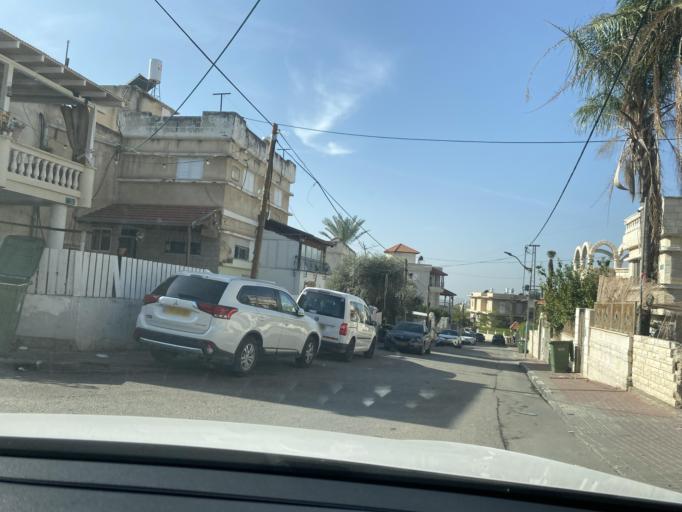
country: IL
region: Central District
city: Kafr Qasim
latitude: 32.1316
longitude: 34.9706
